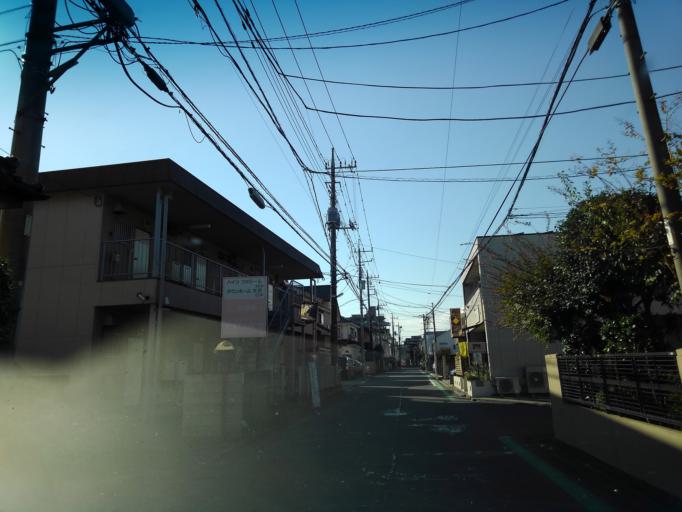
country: JP
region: Saitama
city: Tokorozawa
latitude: 35.7963
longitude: 139.4373
